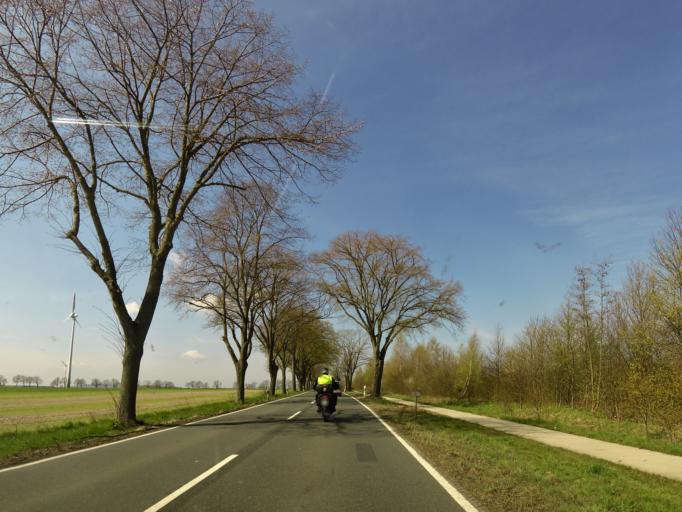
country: DE
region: Lower Saxony
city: Haste
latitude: 52.4329
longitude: 9.3819
